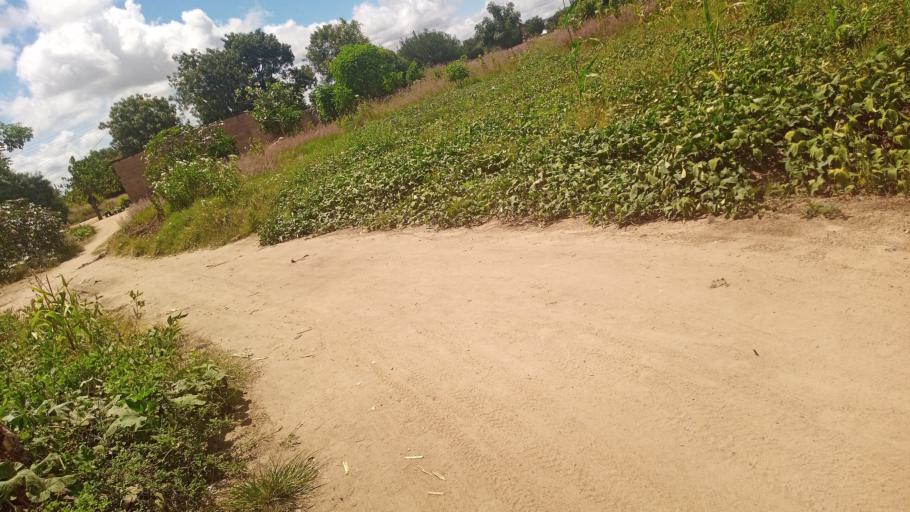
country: TZ
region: Dodoma
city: Kisasa
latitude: -6.1779
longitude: 35.7681
